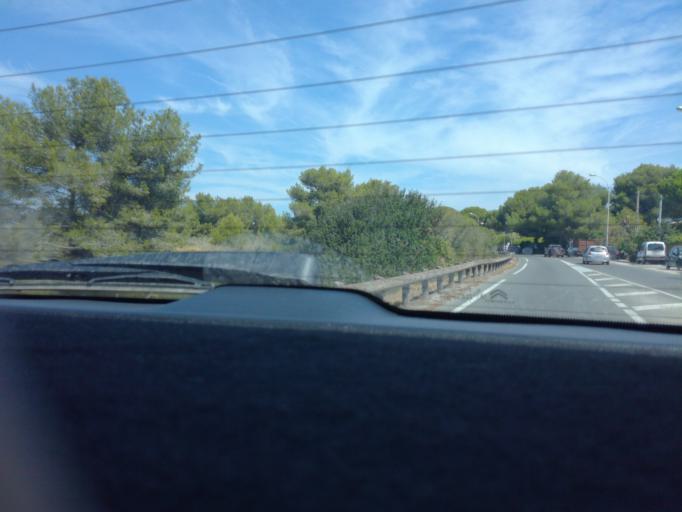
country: FR
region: Provence-Alpes-Cote d'Azur
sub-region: Departement du Var
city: Hyeres
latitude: 43.0730
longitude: 6.1482
